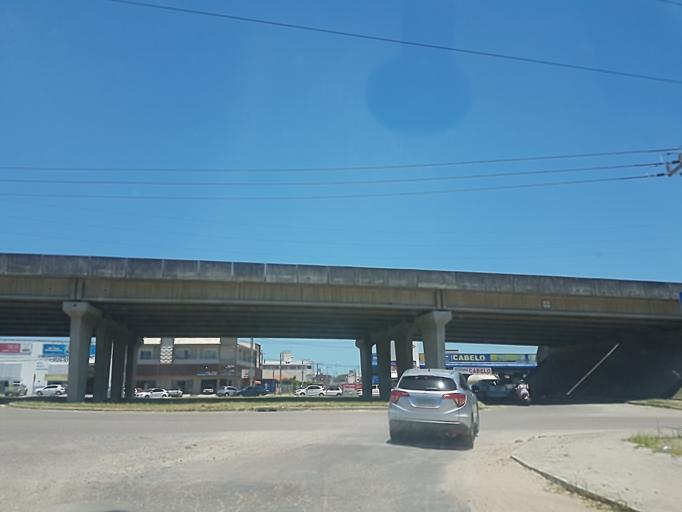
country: BR
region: Santa Catarina
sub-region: Tubarao
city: Tubarao
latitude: -28.4760
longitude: -49.0301
